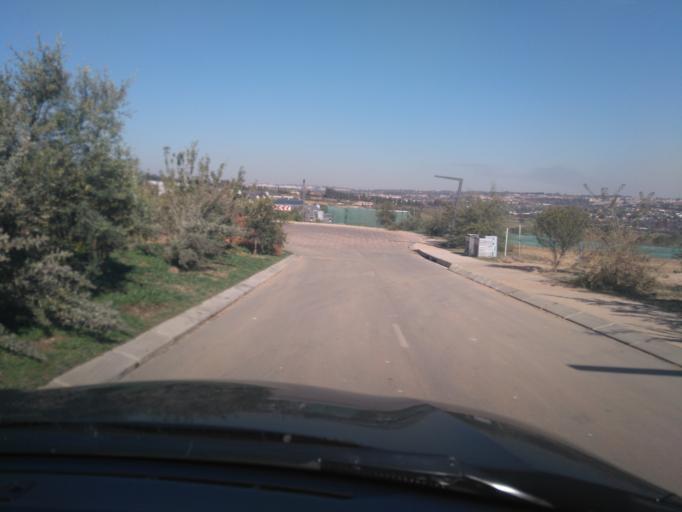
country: ZA
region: Gauteng
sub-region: City of Johannesburg Metropolitan Municipality
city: Diepsloot
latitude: -25.9686
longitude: 27.9976
